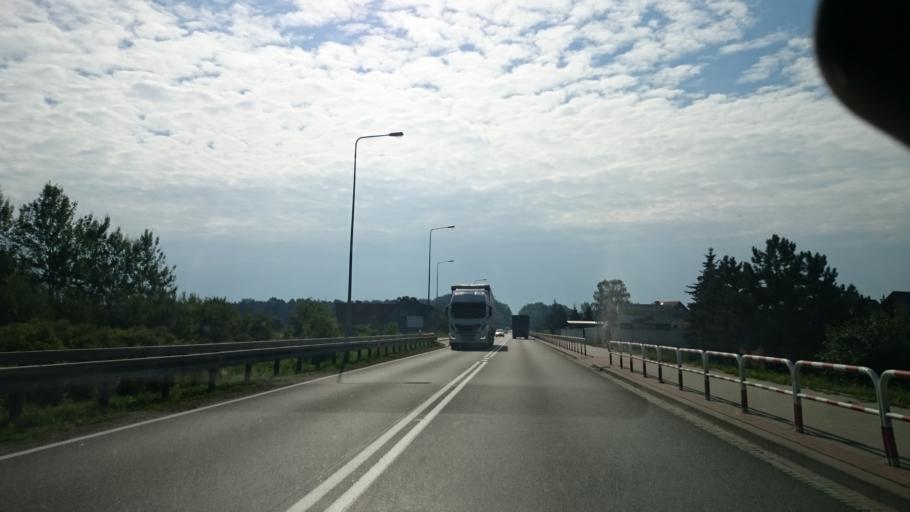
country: PL
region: Opole Voivodeship
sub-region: Powiat strzelecki
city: Strzelce Opolskie
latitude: 50.5048
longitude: 18.3247
